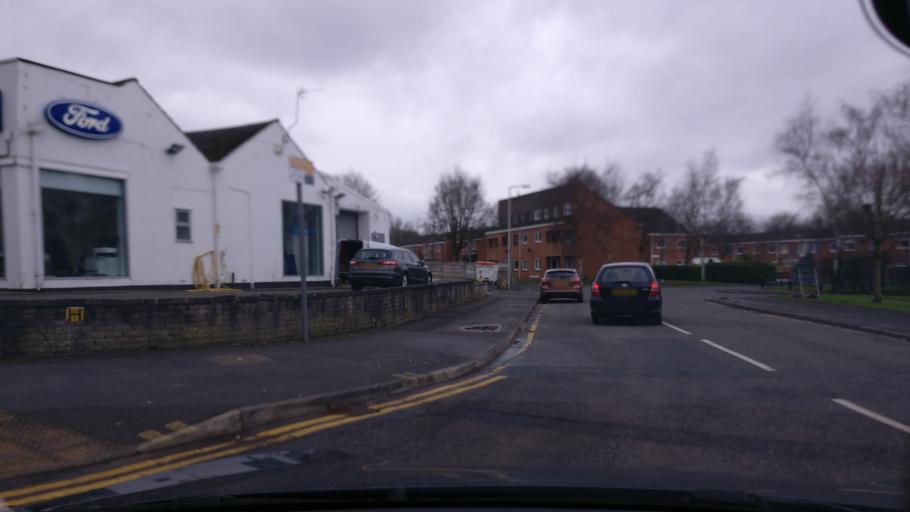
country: GB
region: England
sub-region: Borough of Stockport
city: Hazel Grove
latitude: 53.3732
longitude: -2.1080
